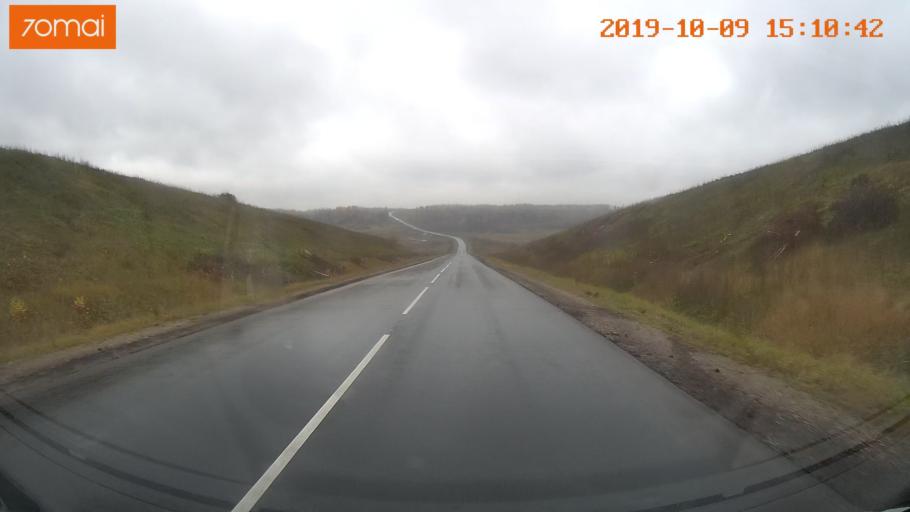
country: RU
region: Kostroma
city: Susanino
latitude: 58.1747
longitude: 41.6374
